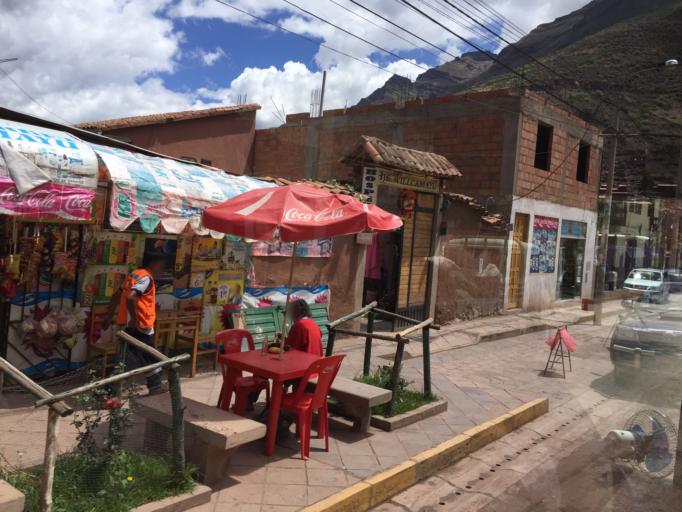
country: PE
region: Cusco
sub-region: Provincia de Calca
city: Pisac
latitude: -13.4219
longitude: -71.8487
